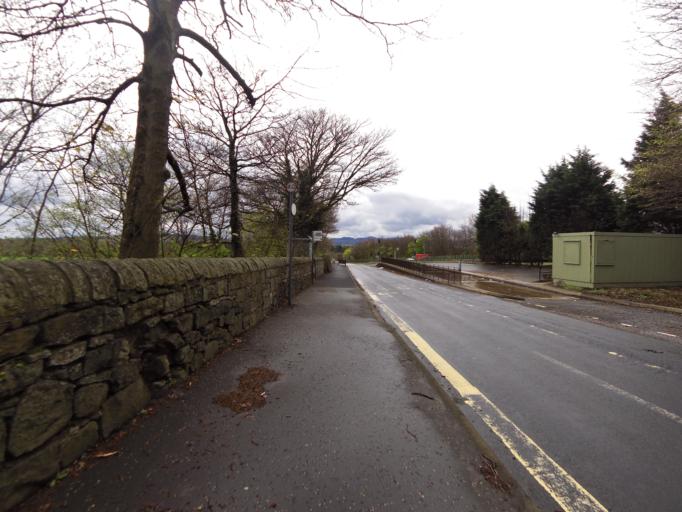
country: GB
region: Scotland
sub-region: Edinburgh
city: Currie
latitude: 55.9683
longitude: -3.3218
